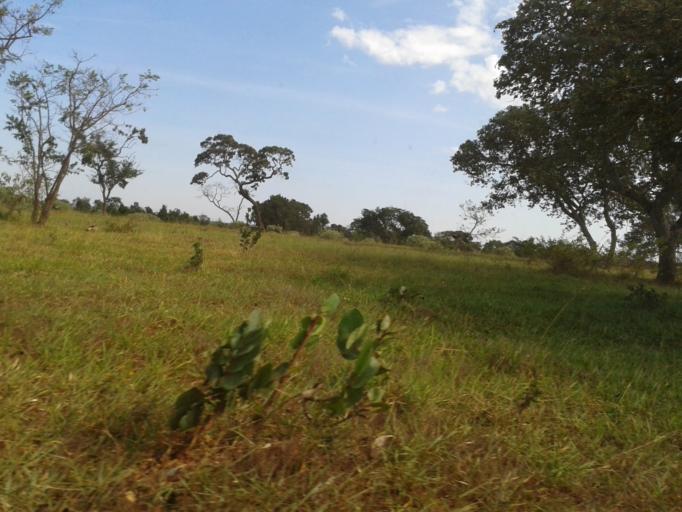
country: BR
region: Minas Gerais
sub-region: Ituiutaba
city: Ituiutaba
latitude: -19.0640
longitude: -49.3644
